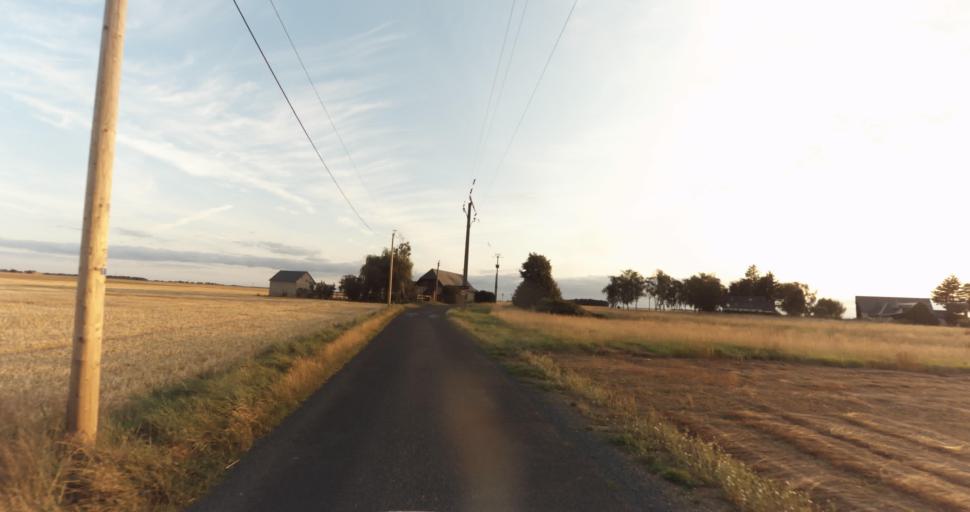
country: FR
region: Haute-Normandie
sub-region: Departement de l'Eure
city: La Madeleine-de-Nonancourt
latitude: 48.8907
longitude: 1.2171
